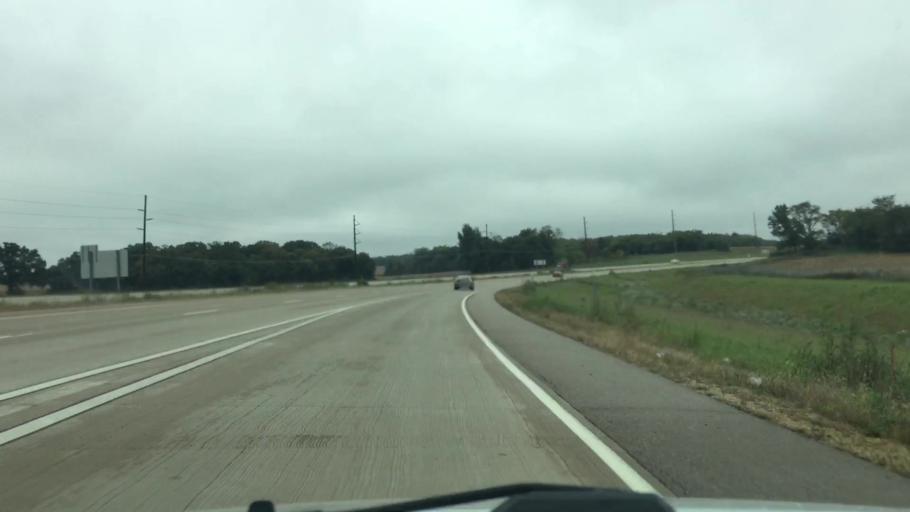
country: US
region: Wisconsin
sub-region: Rock County
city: Milton
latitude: 42.7650
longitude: -88.9256
